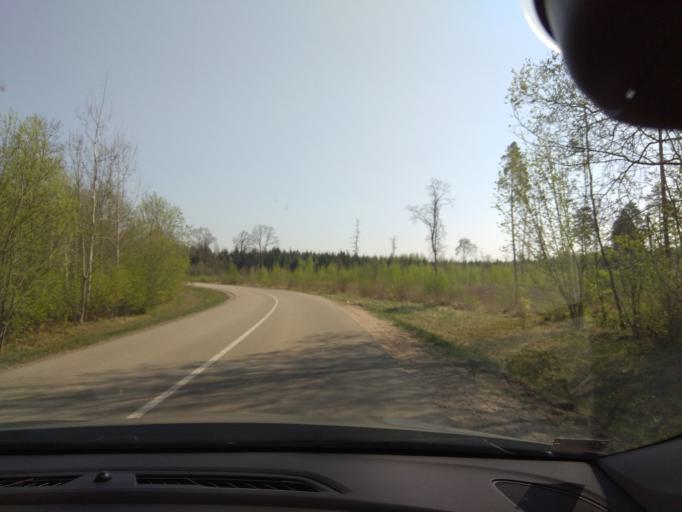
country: LT
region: Panevezys
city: Pasvalys
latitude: 55.9778
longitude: 24.1902
